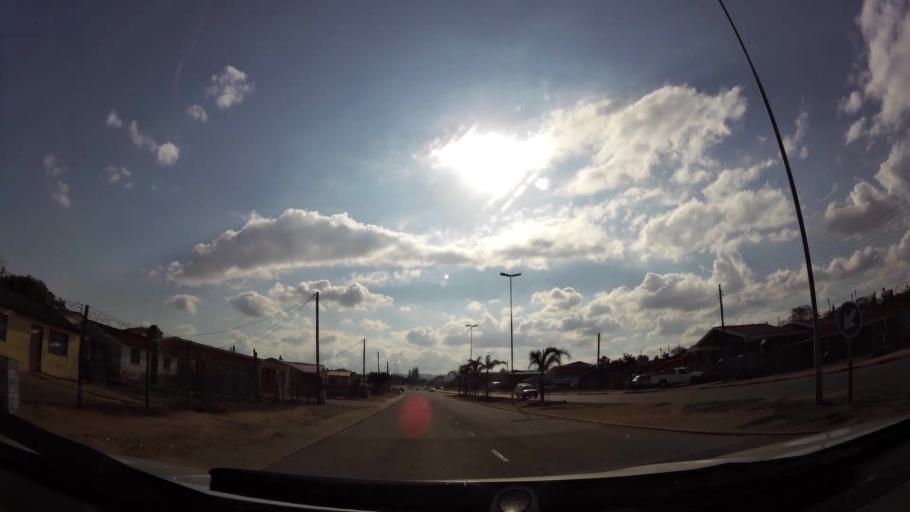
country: ZA
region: Eastern Cape
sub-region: Nelson Mandela Bay Metropolitan Municipality
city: Uitenhage
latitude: -33.7416
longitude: 25.3758
